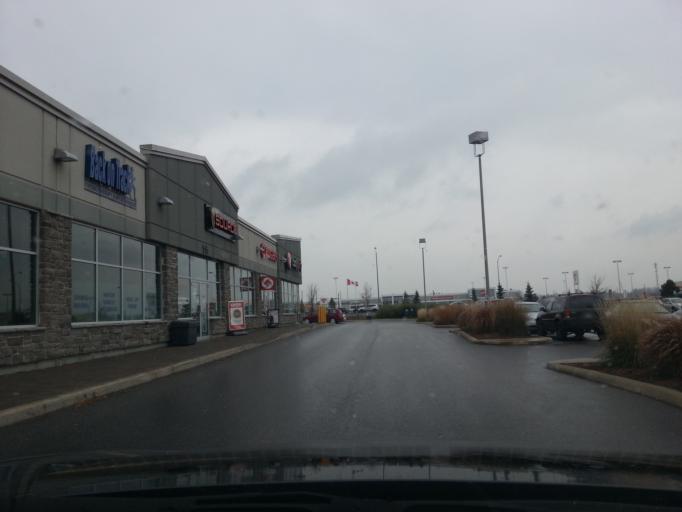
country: CA
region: Ontario
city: Carleton Place
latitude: 45.1317
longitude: -76.1186
